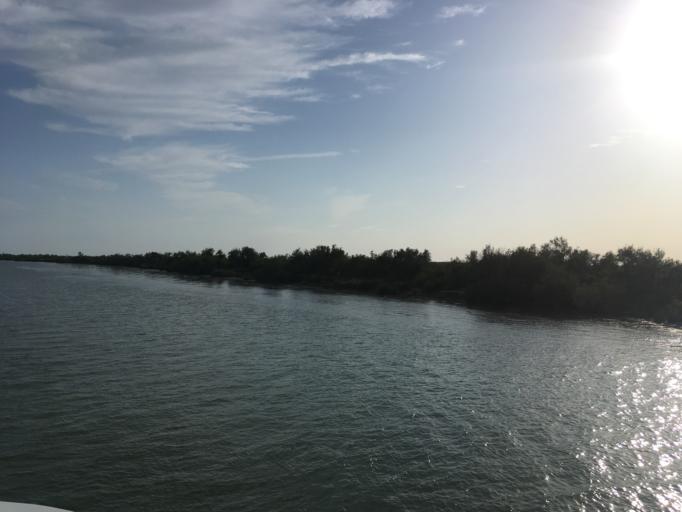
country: FR
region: Provence-Alpes-Cote d'Azur
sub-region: Departement des Bouches-du-Rhone
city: Saintes-Maries-de-la-Mer
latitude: 43.4642
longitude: 4.3922
